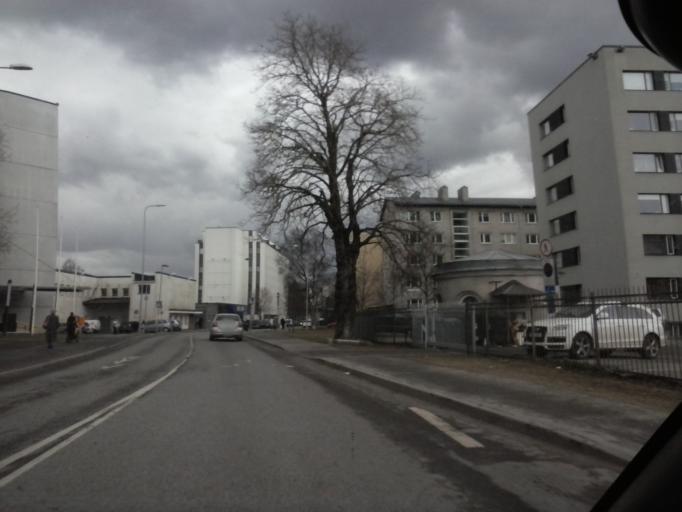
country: EE
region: Harju
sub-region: Tallinna linn
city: Tallinn
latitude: 59.4308
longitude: 24.7924
